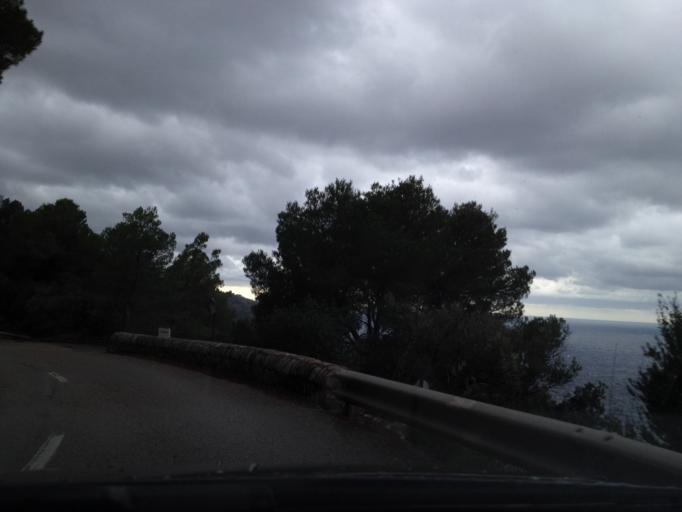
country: ES
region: Balearic Islands
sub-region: Illes Balears
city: Deia
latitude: 39.7735
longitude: 2.6701
